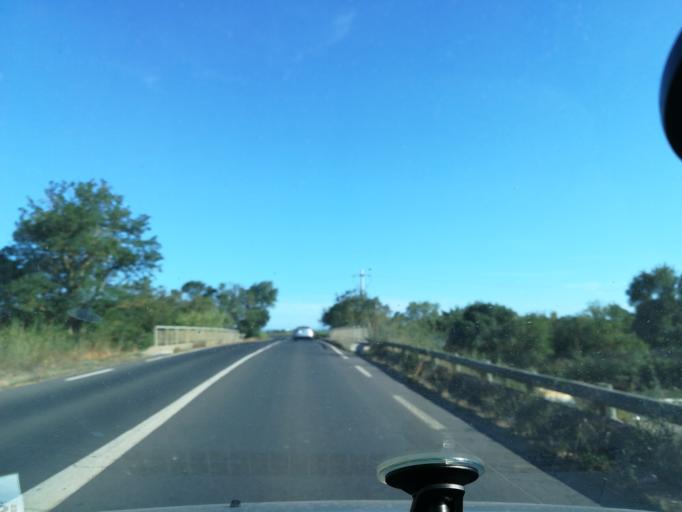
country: FR
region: Languedoc-Roussillon
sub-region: Departement de l'Herault
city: Portiragnes
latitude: 43.2907
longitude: 3.3621
